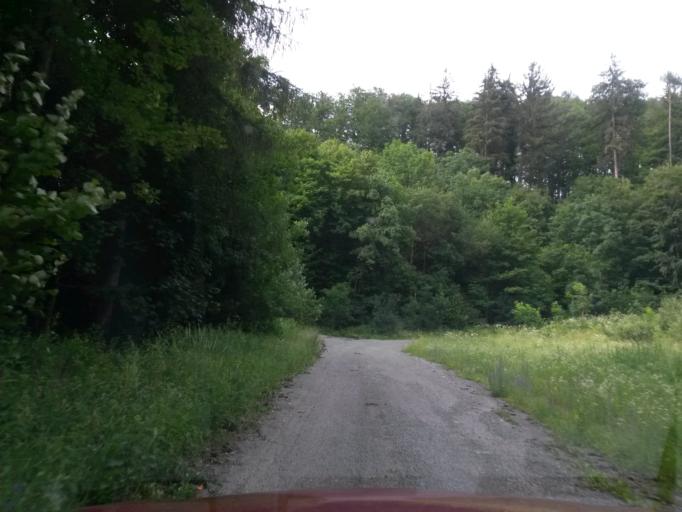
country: SK
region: Banskobystricky
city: Detva
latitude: 48.4739
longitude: 19.2961
